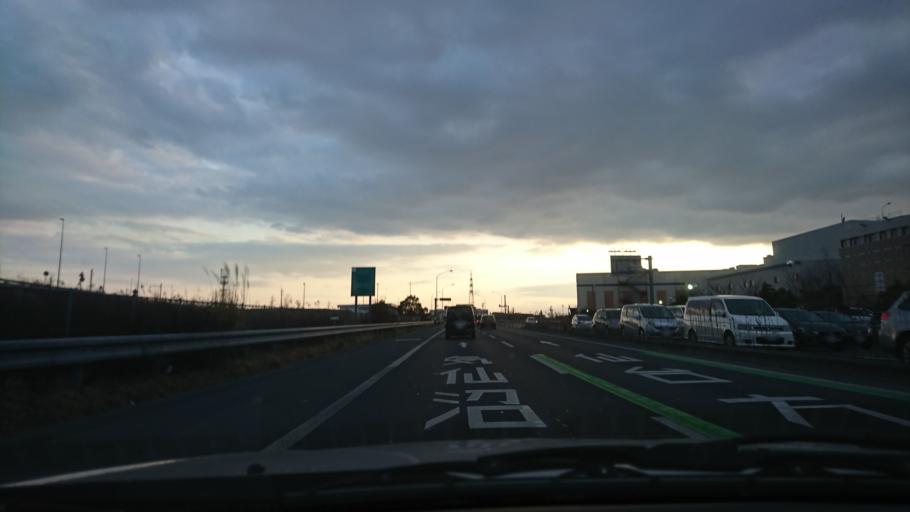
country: JP
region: Miyagi
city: Ishinomaki
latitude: 38.4485
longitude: 141.2689
